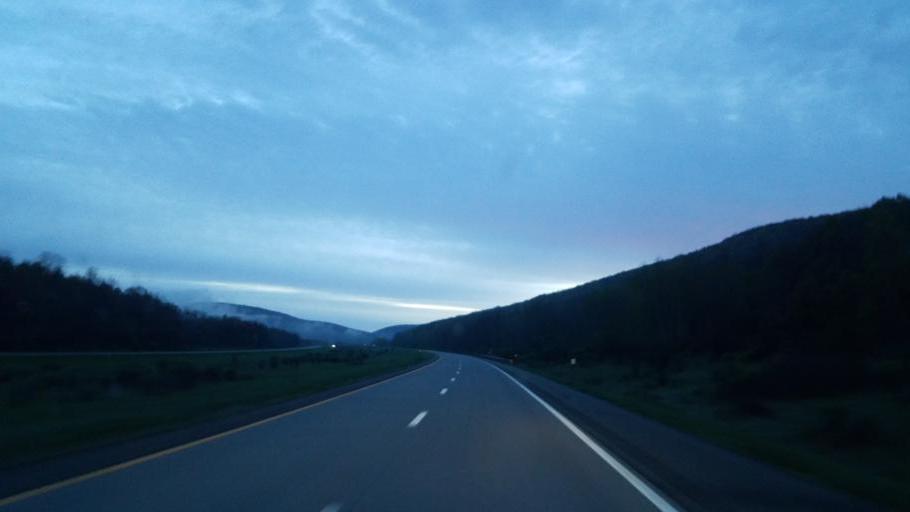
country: US
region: New York
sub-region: Allegany County
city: Cuba
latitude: 42.1941
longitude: -78.3351
